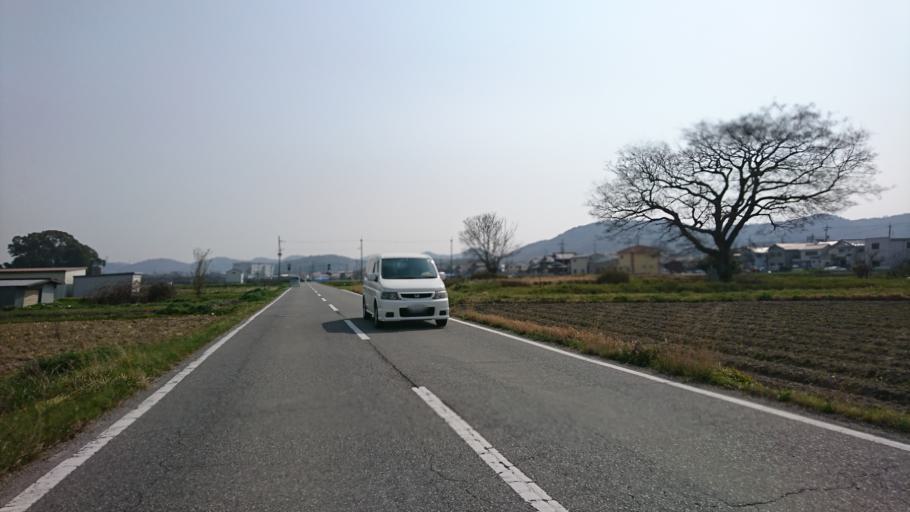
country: JP
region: Hyogo
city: Ono
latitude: 34.8589
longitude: 134.9122
